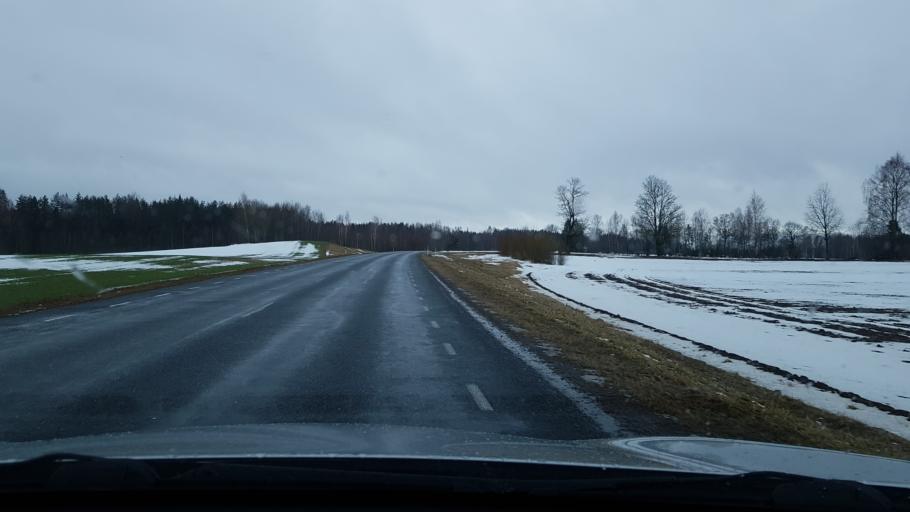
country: LV
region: Apes Novads
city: Ape
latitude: 57.6729
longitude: 26.7236
